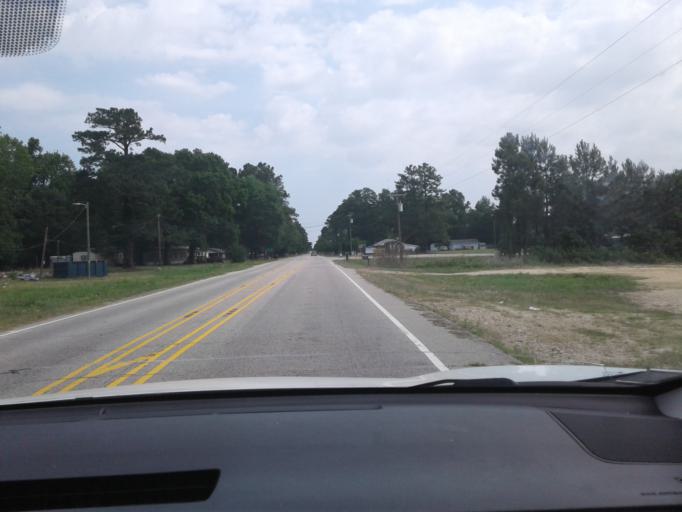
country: US
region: North Carolina
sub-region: Harnett County
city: Erwin
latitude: 35.3497
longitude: -78.6675
